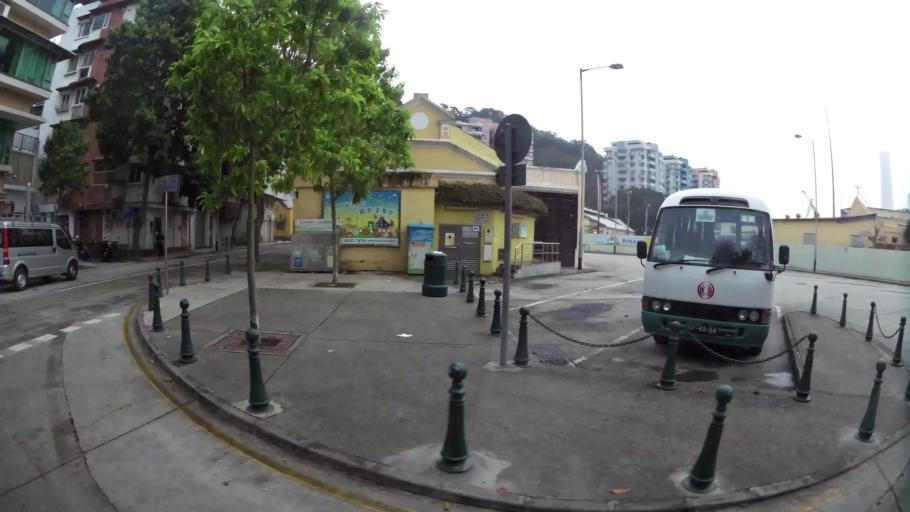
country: CN
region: Guangdong
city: Wanzai
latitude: 22.1855
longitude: 113.5313
